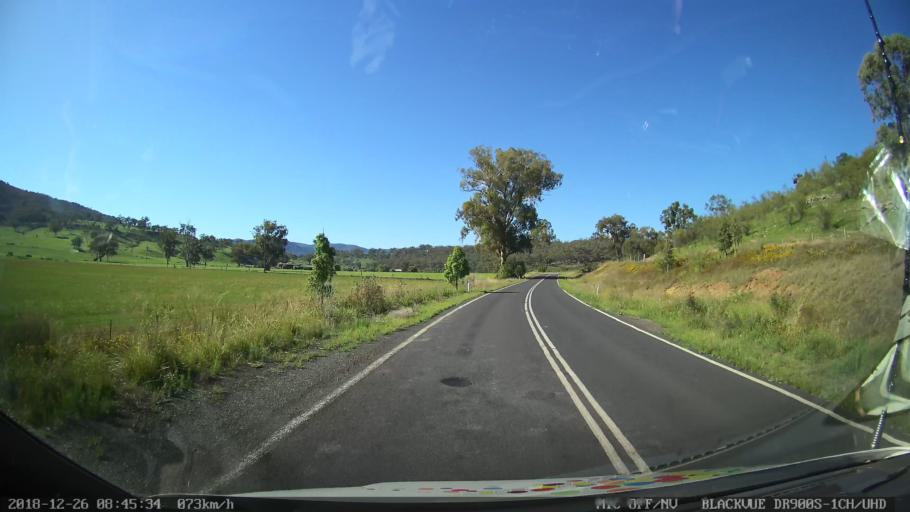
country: AU
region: New South Wales
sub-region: Mid-Western Regional
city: Kandos
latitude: -32.5266
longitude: 150.0870
